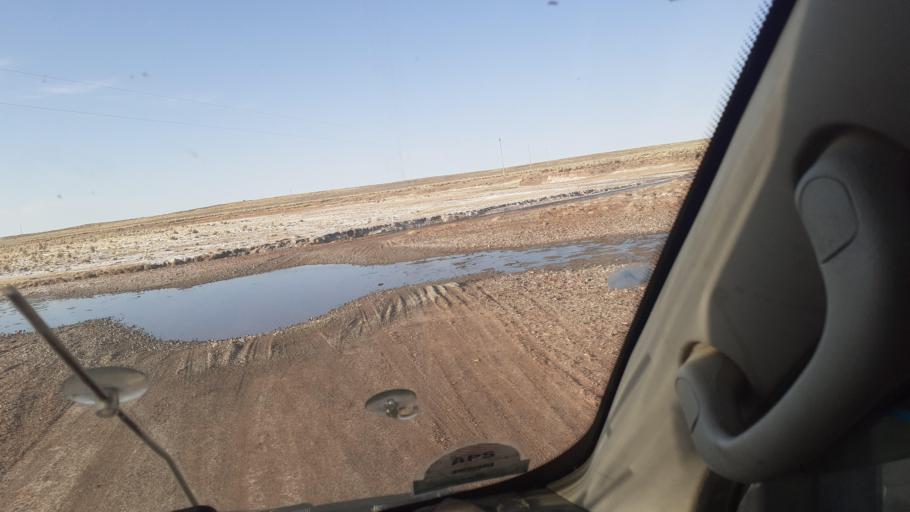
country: BO
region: La Paz
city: Tiahuanaco
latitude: -17.0004
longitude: -68.7264
